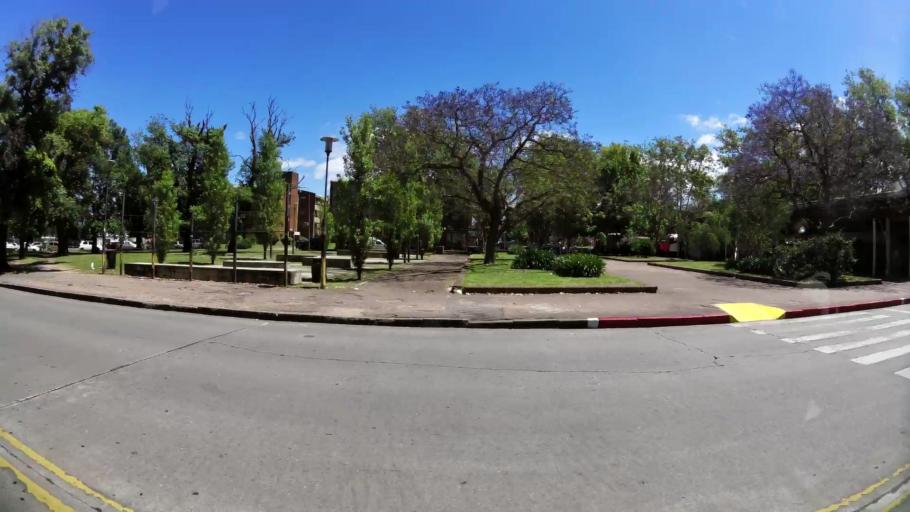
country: UY
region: Montevideo
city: Montevideo
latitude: -34.8992
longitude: -56.1281
